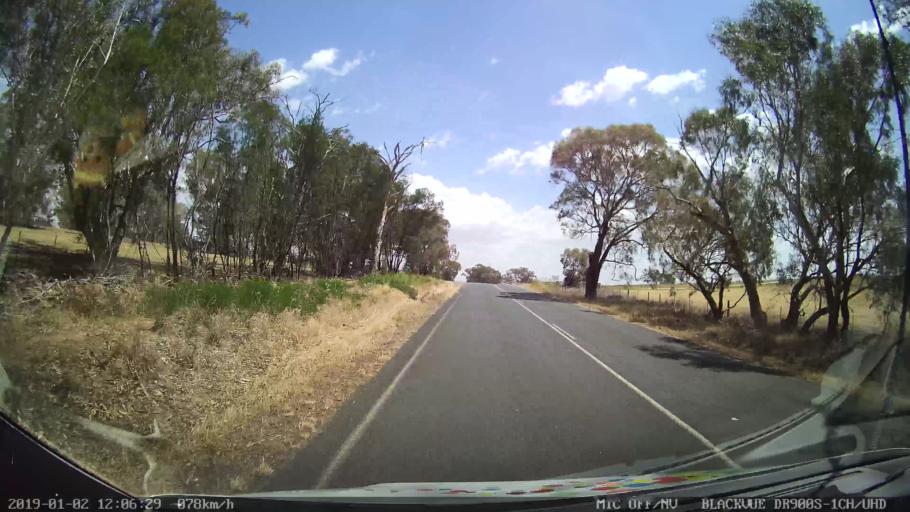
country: AU
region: New South Wales
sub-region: Young
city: Young
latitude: -34.5029
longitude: 148.2941
